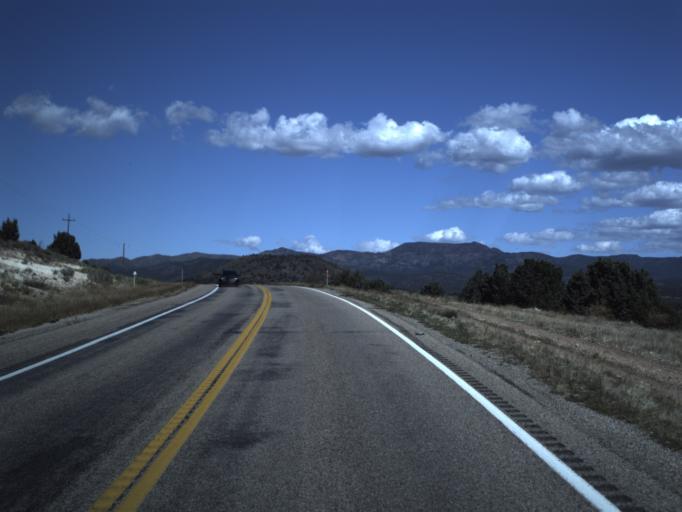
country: US
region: Utah
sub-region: Washington County
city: Ivins
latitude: 37.3748
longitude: -113.6567
